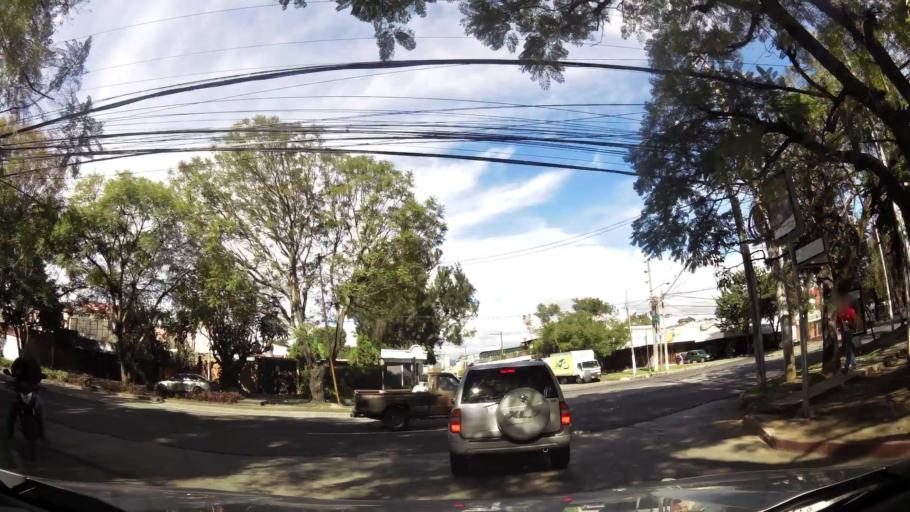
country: GT
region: Guatemala
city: Santa Catarina Pinula
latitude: 14.5882
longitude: -90.5218
